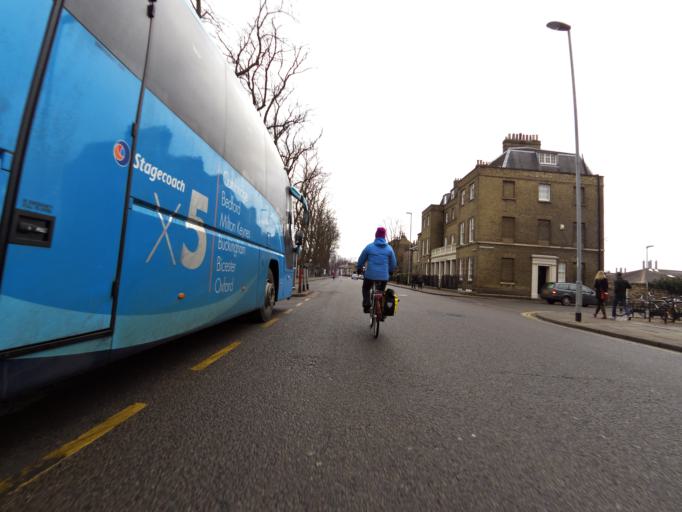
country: GB
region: England
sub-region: Cambridgeshire
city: Cambridge
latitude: 52.2031
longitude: 0.1299
